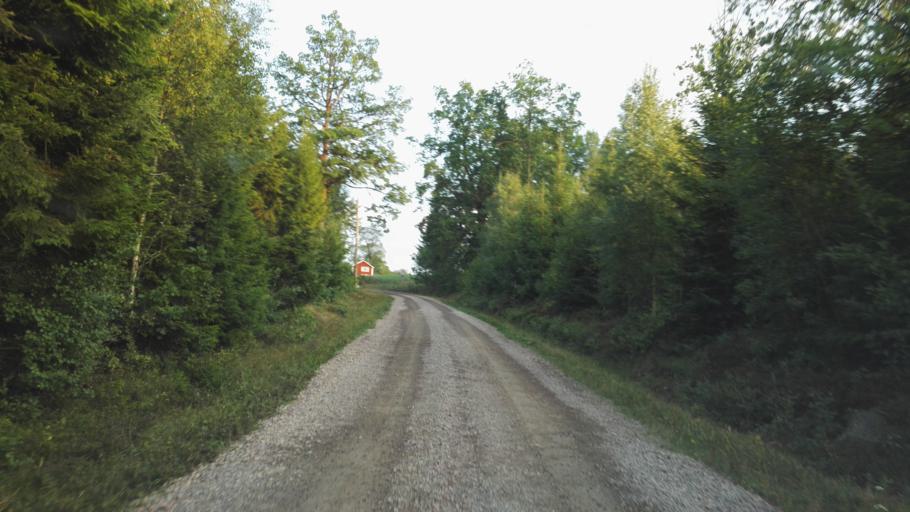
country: SE
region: Joenkoeping
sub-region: Vetlanda Kommun
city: Landsbro
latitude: 57.2509
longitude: 14.8849
